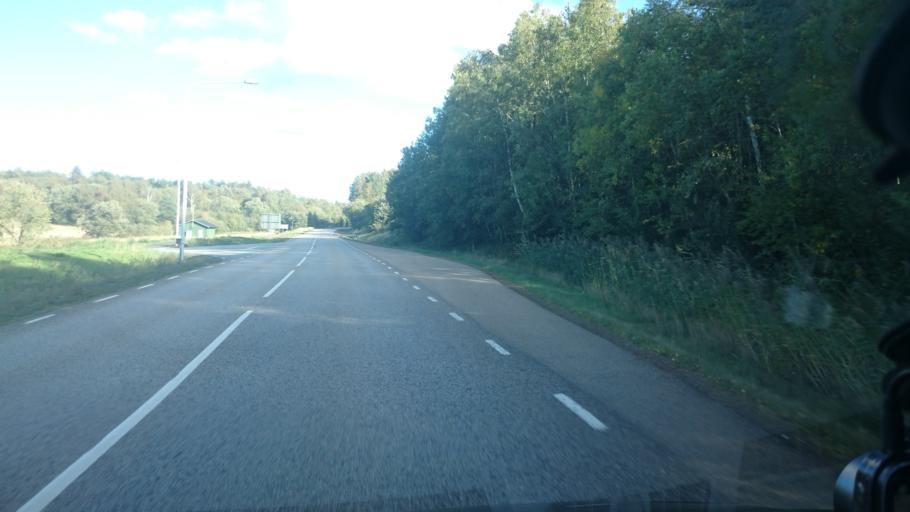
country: SE
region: Vaestra Goetaland
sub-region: Lysekils Kommun
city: Lysekil
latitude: 58.3350
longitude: 11.4262
